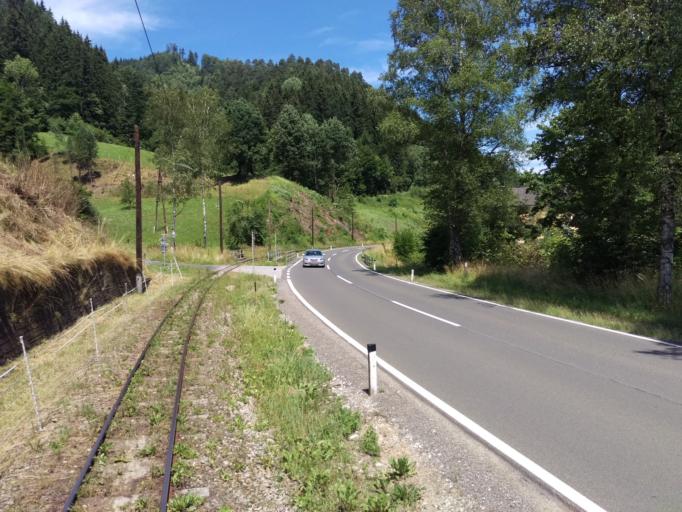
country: AT
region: Styria
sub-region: Politischer Bezirk Bruck-Muerzzuschlag
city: Pernegg an der Mur
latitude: 47.3800
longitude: 15.4005
